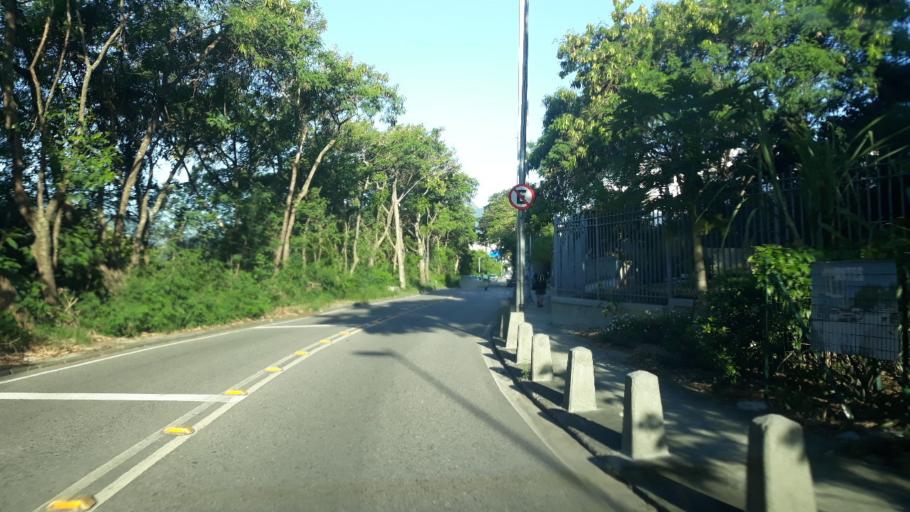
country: BR
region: Rio de Janeiro
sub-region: Rio De Janeiro
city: Rio de Janeiro
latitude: -22.9965
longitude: -43.3535
